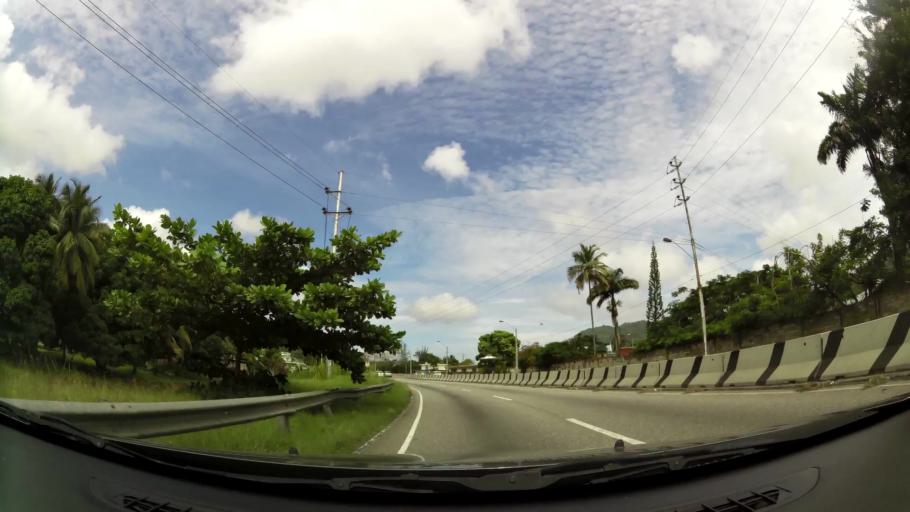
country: TT
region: Diego Martin
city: Petit Valley
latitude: 10.6971
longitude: -61.5539
